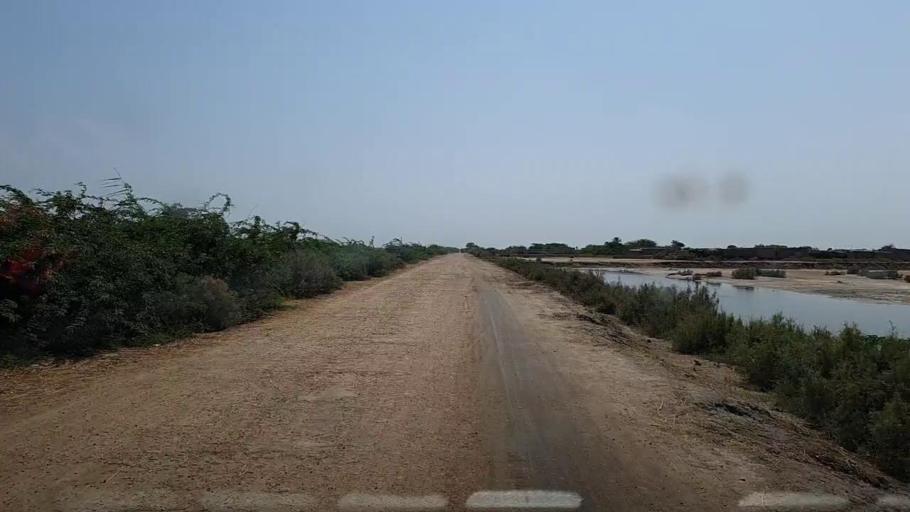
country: PK
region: Sindh
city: Mirpur Batoro
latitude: 24.6326
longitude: 68.4522
